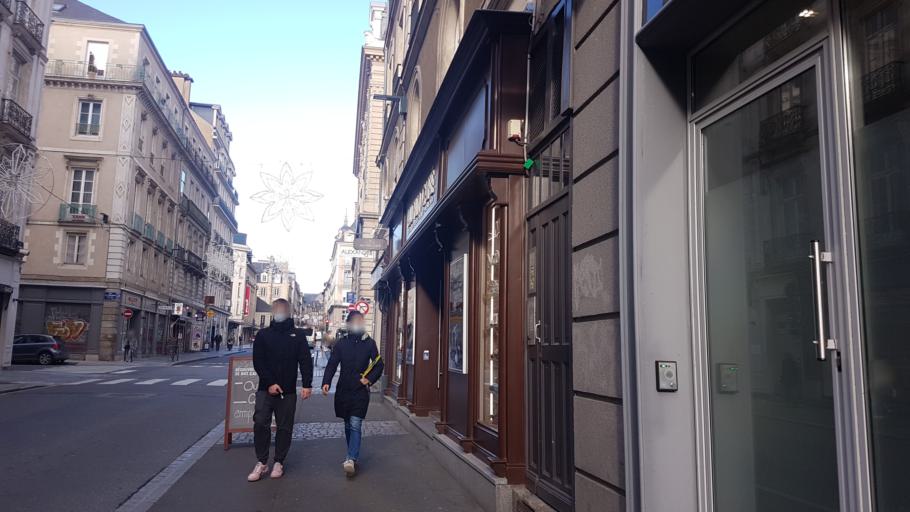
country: FR
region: Brittany
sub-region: Departement d'Ille-et-Vilaine
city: Rennes
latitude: 48.1090
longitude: -1.6802
